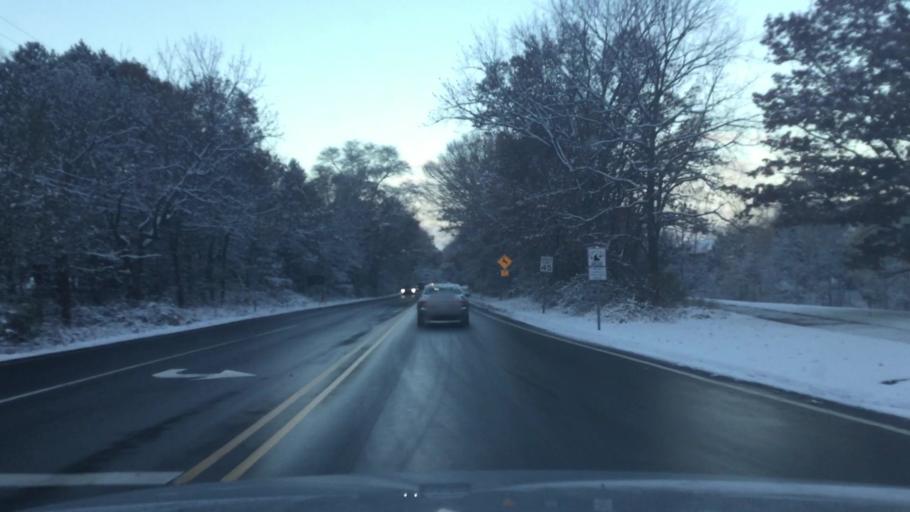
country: US
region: Michigan
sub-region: Oakland County
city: West Bloomfield Township
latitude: 42.5919
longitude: -83.4323
